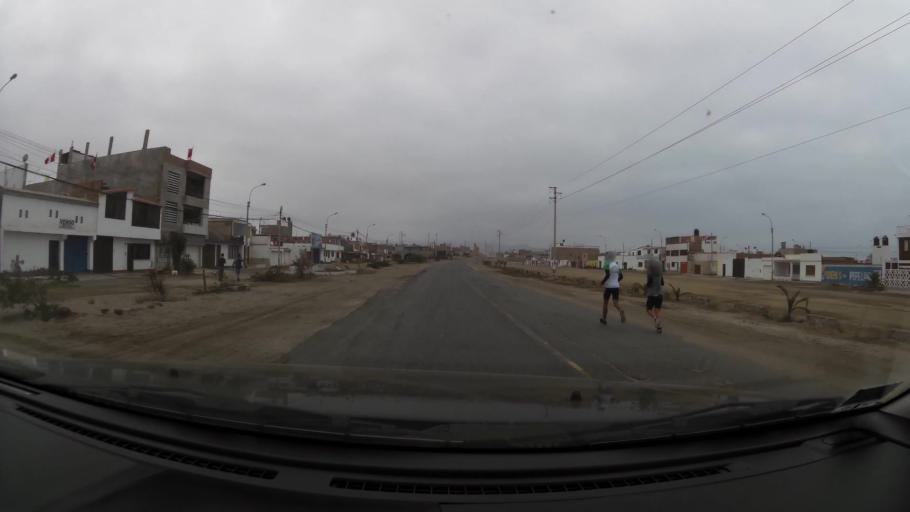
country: PE
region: Lima
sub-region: Lima
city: San Bartolo
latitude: -12.3600
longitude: -76.7986
